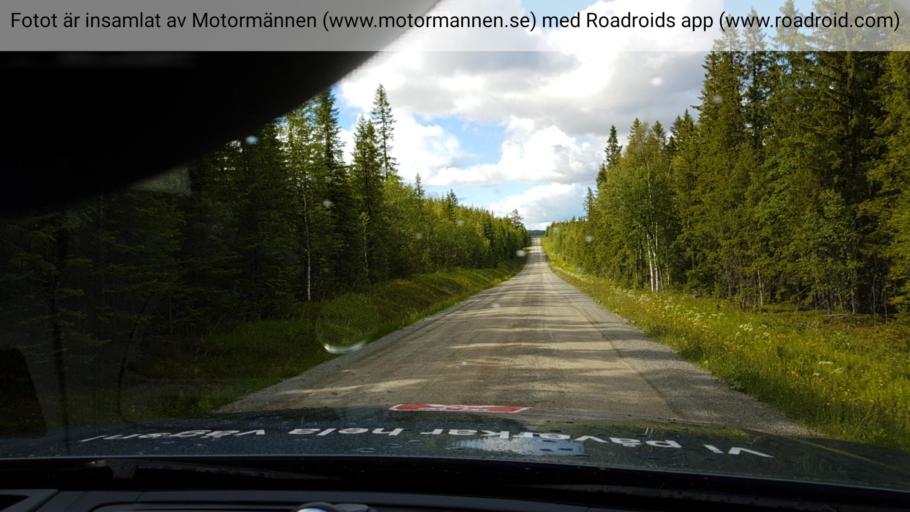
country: SE
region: Jaemtland
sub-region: Bergs Kommun
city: Hoverberg
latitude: 63.0203
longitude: 14.0864
